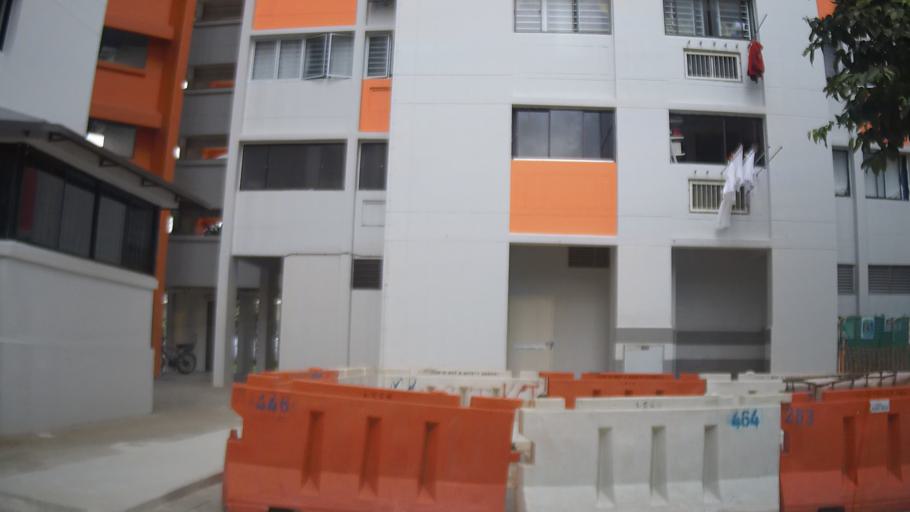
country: MY
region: Johor
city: Johor Bahru
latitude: 1.4319
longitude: 103.7802
